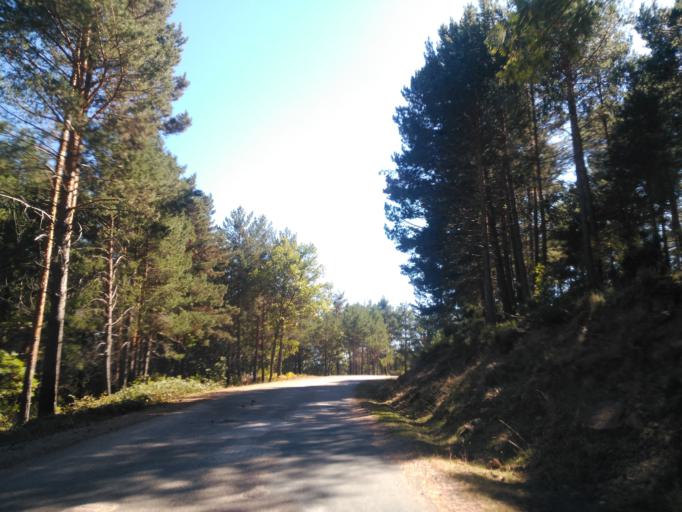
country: ES
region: Castille and Leon
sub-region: Provincia de Soria
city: Vinuesa
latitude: 41.9701
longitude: -2.7930
